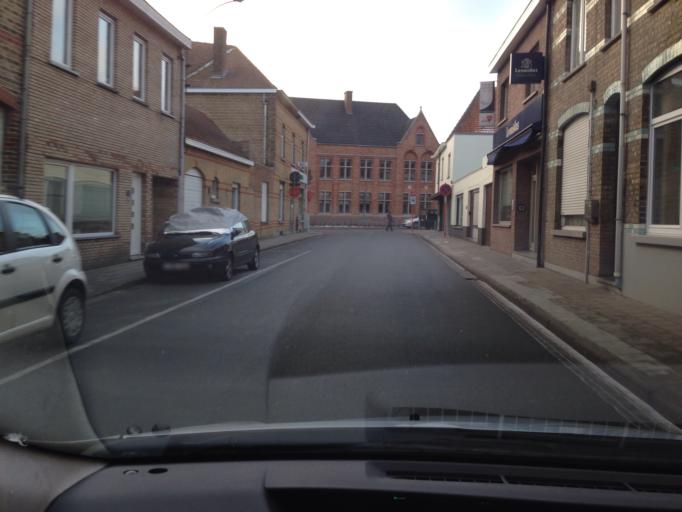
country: BE
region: Flanders
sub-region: Provincie West-Vlaanderen
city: Gistel
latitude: 51.1572
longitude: 2.9691
